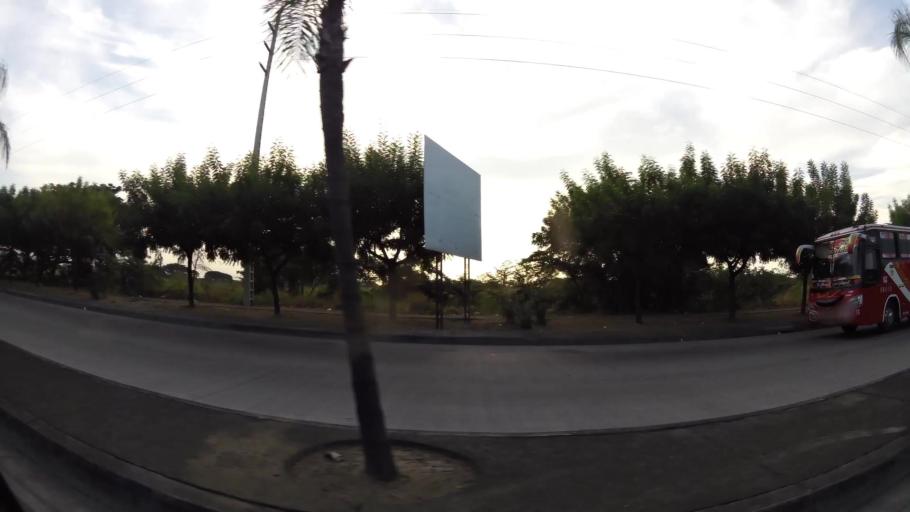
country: EC
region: Guayas
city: Eloy Alfaro
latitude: -2.1031
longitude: -79.8885
